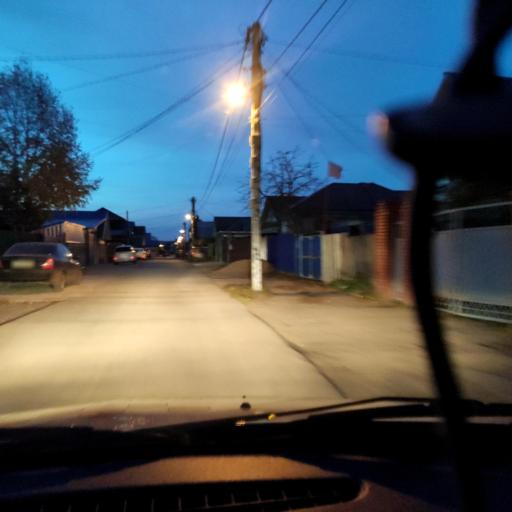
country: RU
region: Bashkortostan
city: Ufa
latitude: 54.7270
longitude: 55.9028
